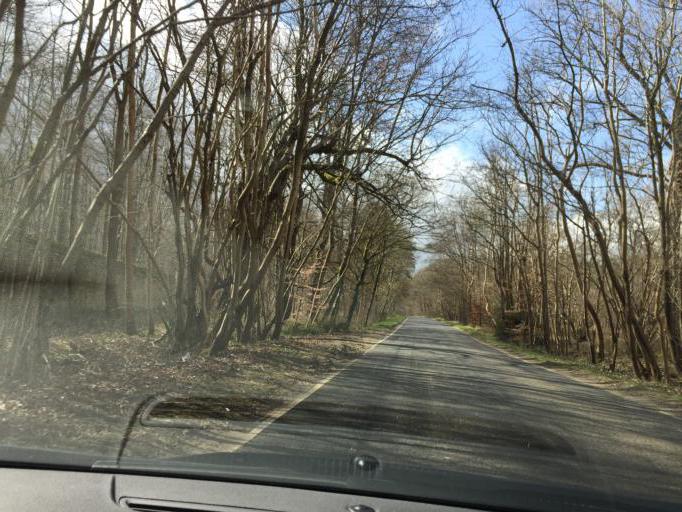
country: GB
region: England
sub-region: Oxfordshire
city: Stonesfield
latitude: 51.8644
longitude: -1.3947
